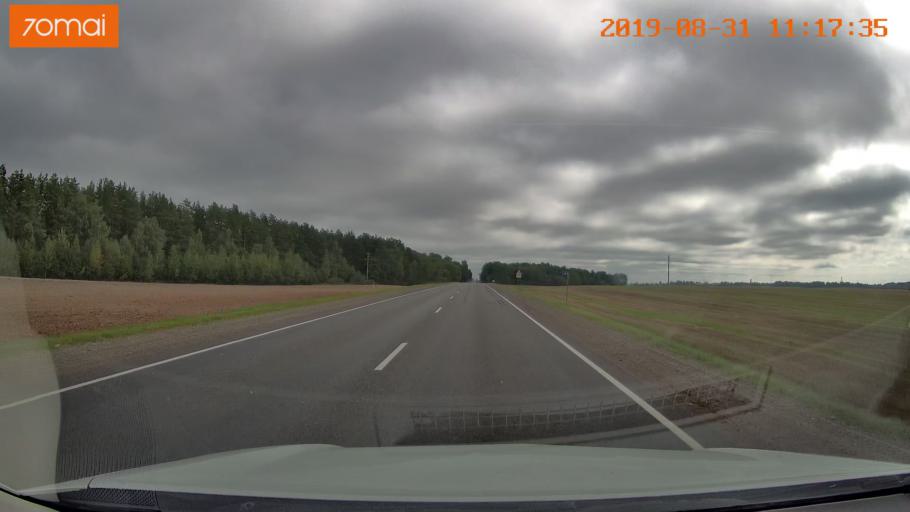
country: BY
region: Mogilev
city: Chavusy
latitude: 53.8057
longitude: 30.9061
